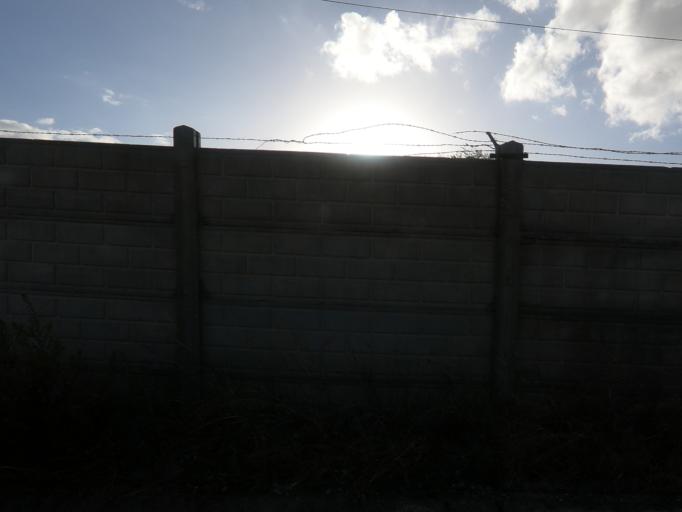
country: PT
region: Setubal
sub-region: Moita
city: Alhos Vedros
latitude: 38.6730
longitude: -9.0454
